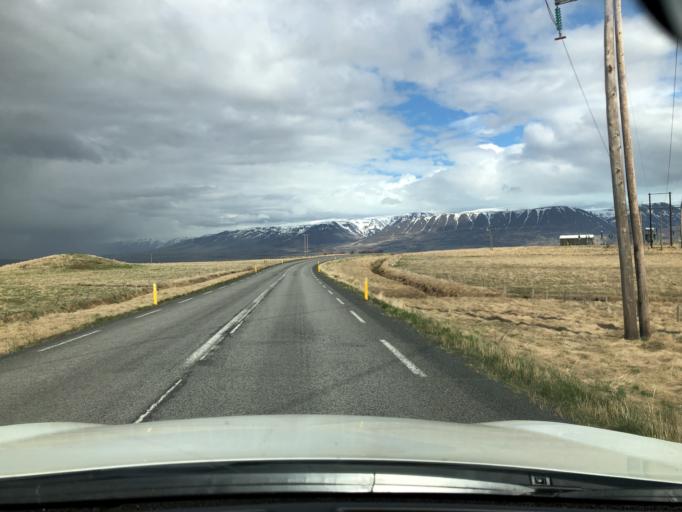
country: IS
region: Northwest
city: Saudarkrokur
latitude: 65.5466
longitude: -19.4926
